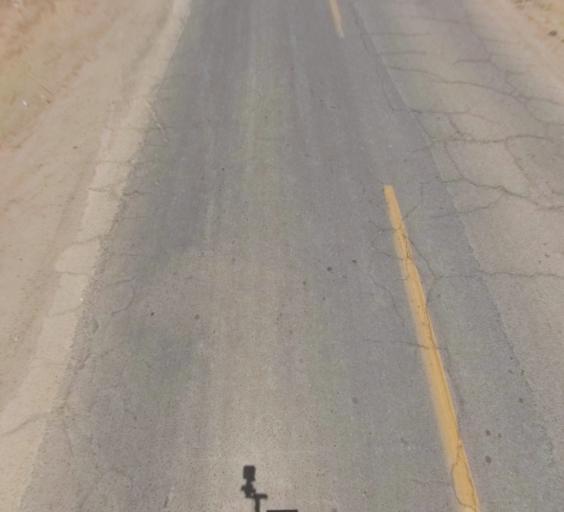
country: US
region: California
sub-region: Madera County
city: Parksdale
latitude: 36.9495
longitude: -120.0285
